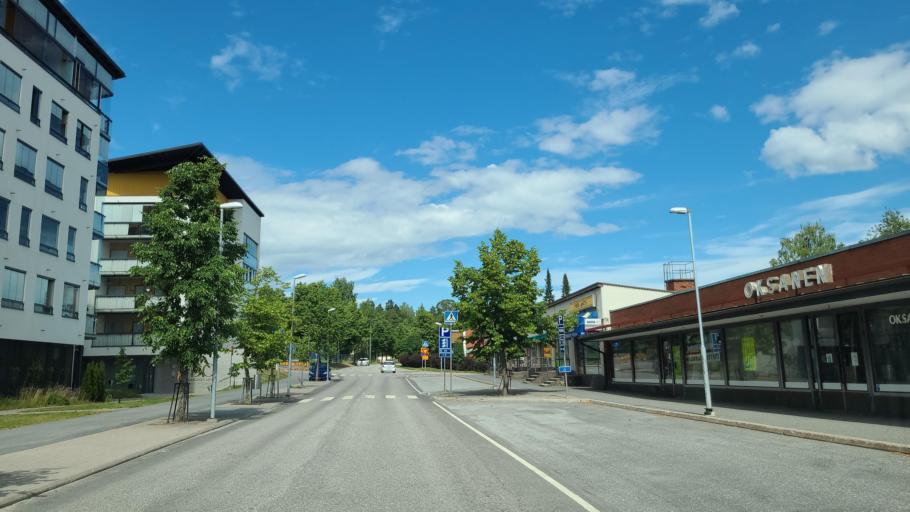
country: FI
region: Central Finland
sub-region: Jyvaeskylae
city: Saeynaetsalo
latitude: 62.2475
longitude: 25.8704
